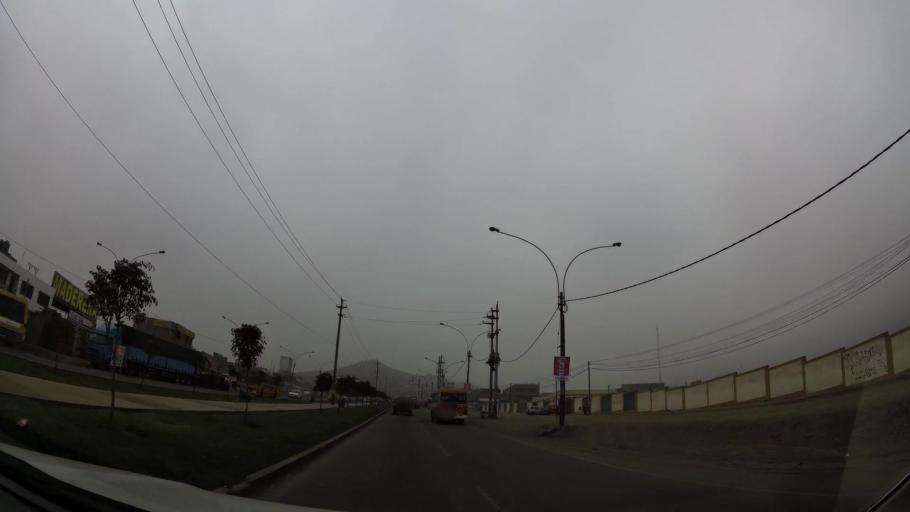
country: PE
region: Lima
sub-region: Lima
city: Urb. Santo Domingo
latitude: -11.9235
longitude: -76.9621
